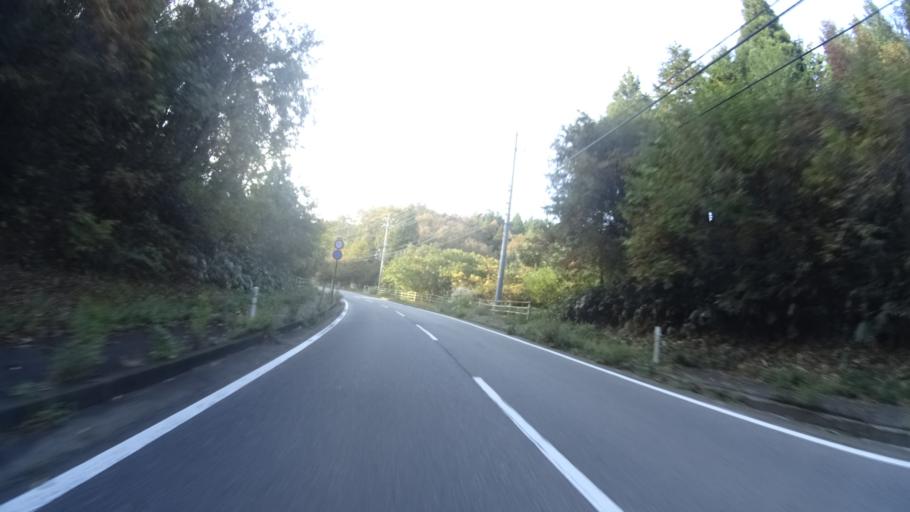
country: JP
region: Ishikawa
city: Hakui
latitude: 37.0653
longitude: 136.7712
